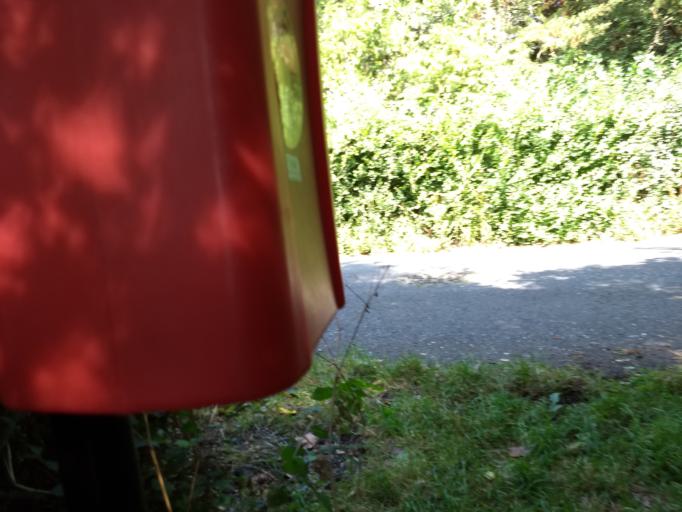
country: GB
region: England
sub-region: Isle of Wight
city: Northwood
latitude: 50.7351
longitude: -1.3203
